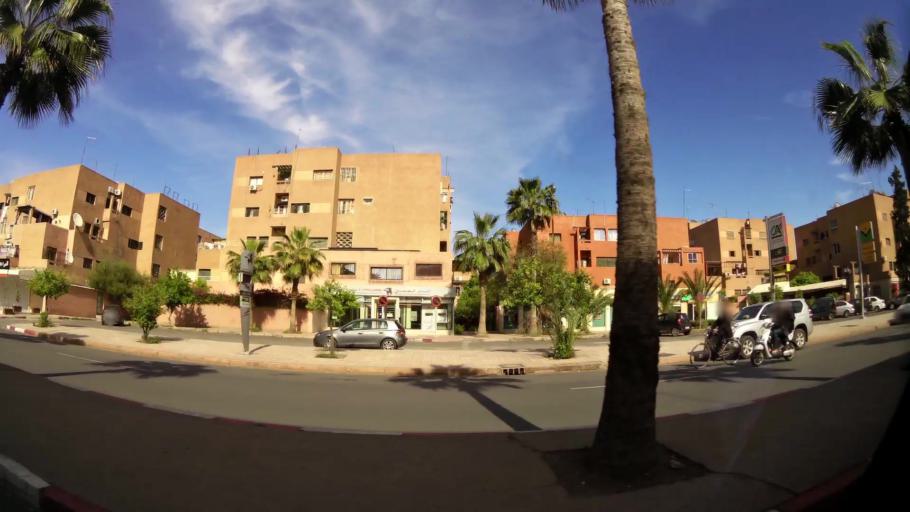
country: MA
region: Marrakech-Tensift-Al Haouz
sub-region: Marrakech
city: Marrakesh
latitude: 31.6451
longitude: -8.0008
